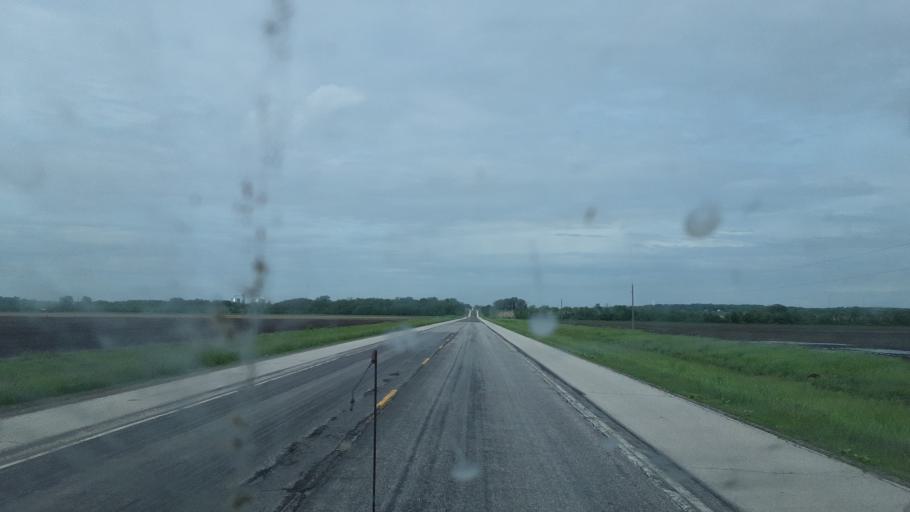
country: US
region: Illinois
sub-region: Hancock County
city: Warsaw
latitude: 40.3945
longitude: -91.5506
